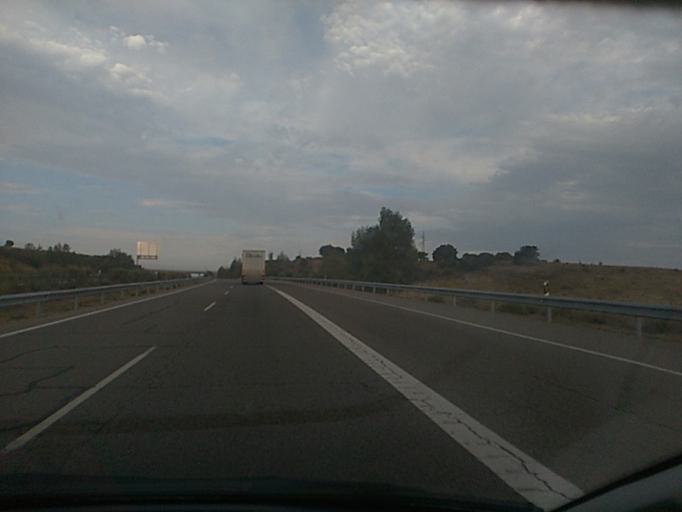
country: ES
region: Castille and Leon
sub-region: Provincia de Zamora
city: Manganeses de la Polvorosa
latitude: 42.0429
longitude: -5.7503
